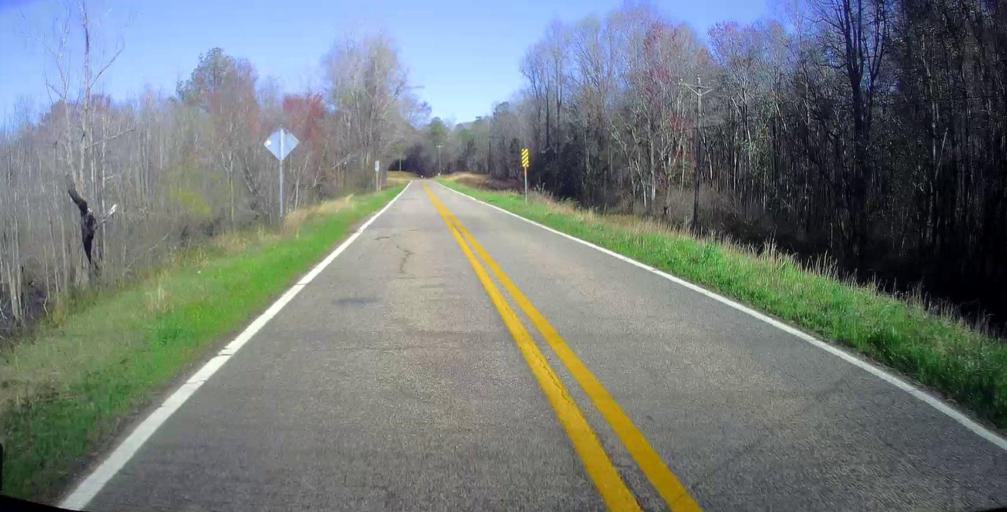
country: US
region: Georgia
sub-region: Peach County
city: Fort Valley
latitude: 32.6464
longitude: -83.8968
